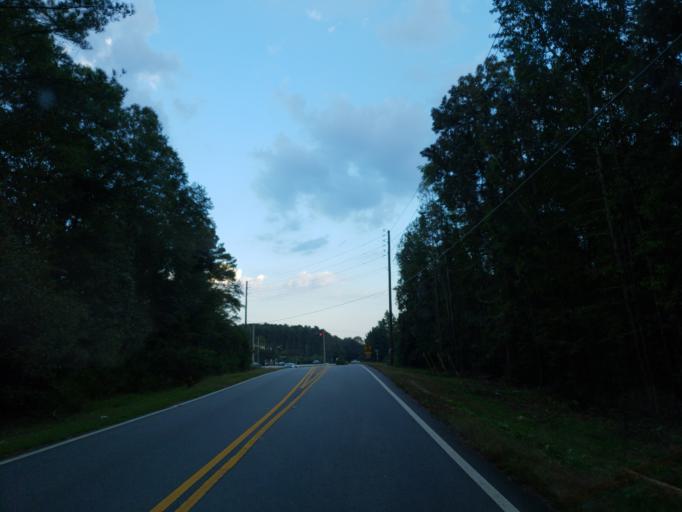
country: US
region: Georgia
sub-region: Cobb County
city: Powder Springs
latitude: 33.8422
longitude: -84.6888
